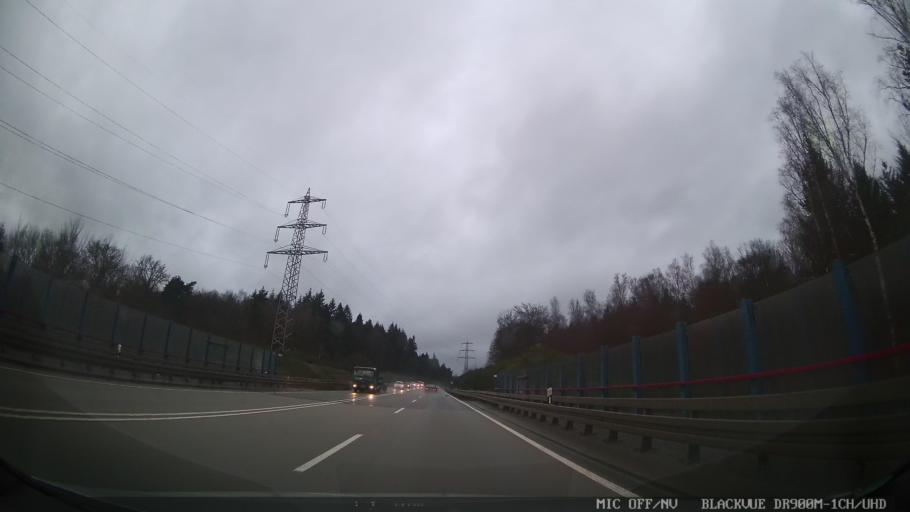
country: DE
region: Saarland
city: Mettlach
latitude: 49.4774
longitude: 6.6273
